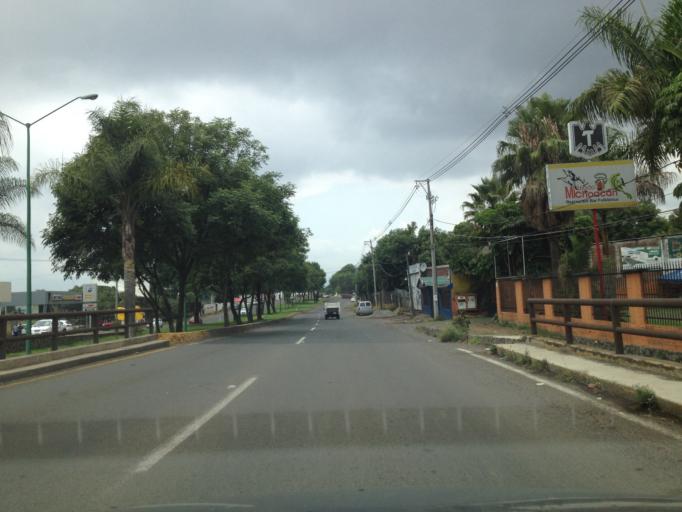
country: MX
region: Michoacan
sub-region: Uruapan
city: Toreo Bajo (El Toreo Bajo)
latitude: 19.4315
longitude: -102.0263
